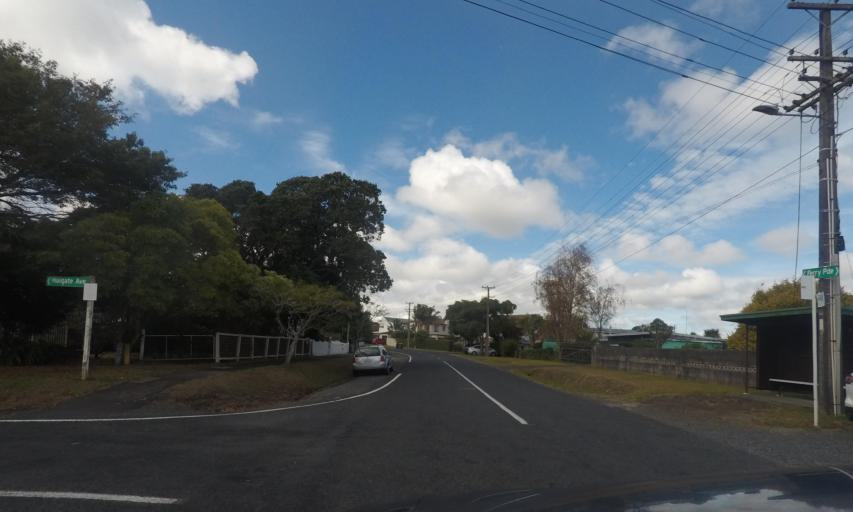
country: NZ
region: Auckland
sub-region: Auckland
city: North Shore
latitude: -36.7799
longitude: 174.6584
